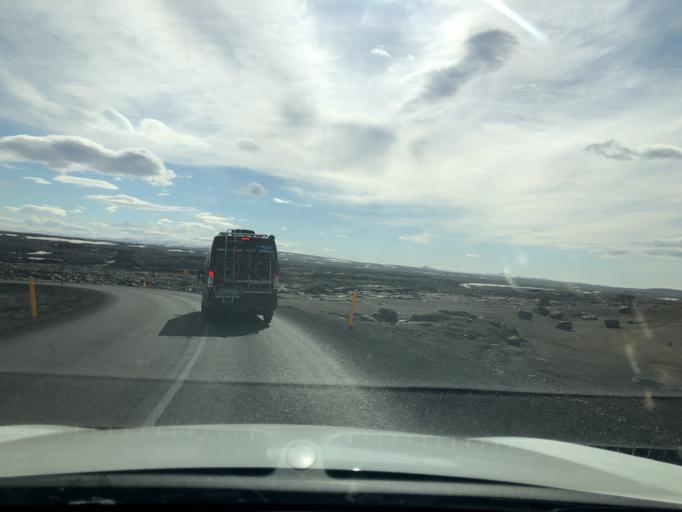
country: IS
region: Northeast
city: Husavik
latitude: 65.8104
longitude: -16.4040
